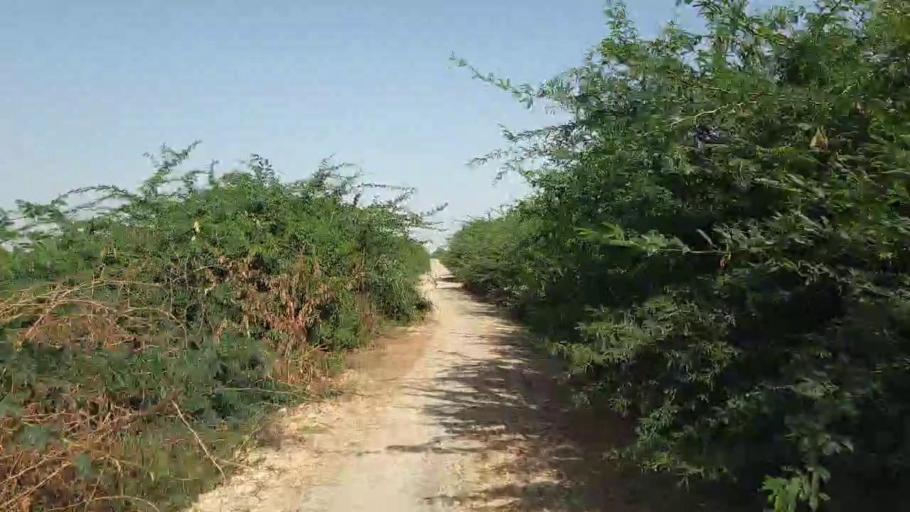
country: PK
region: Sindh
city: Tando Bago
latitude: 24.7205
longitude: 69.0730
